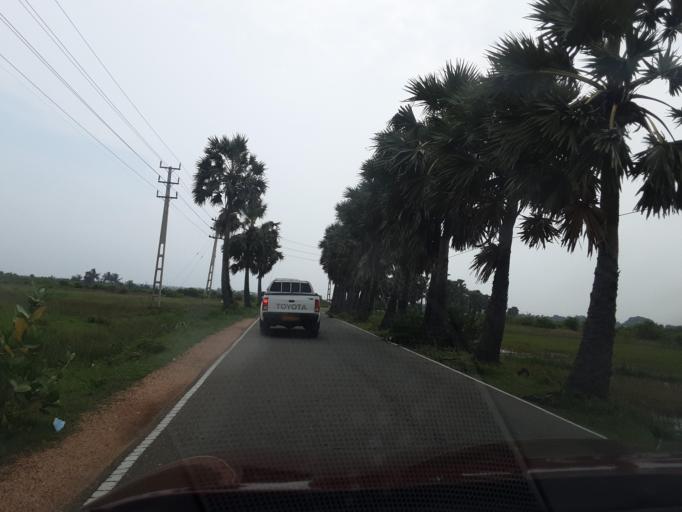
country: LK
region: Northern Province
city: Jaffna
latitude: 9.6662
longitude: 80.0575
